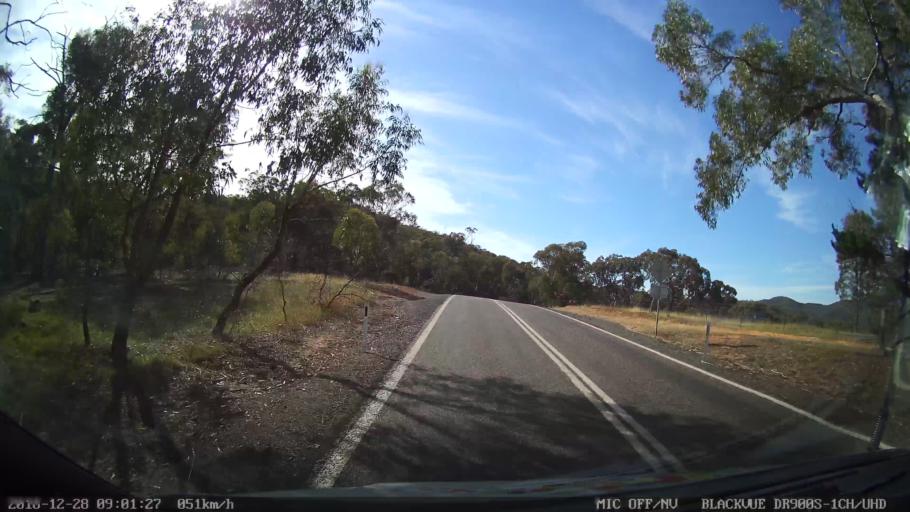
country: AU
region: New South Wales
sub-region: Upper Lachlan Shire
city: Crookwell
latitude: -34.1465
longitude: 149.3336
